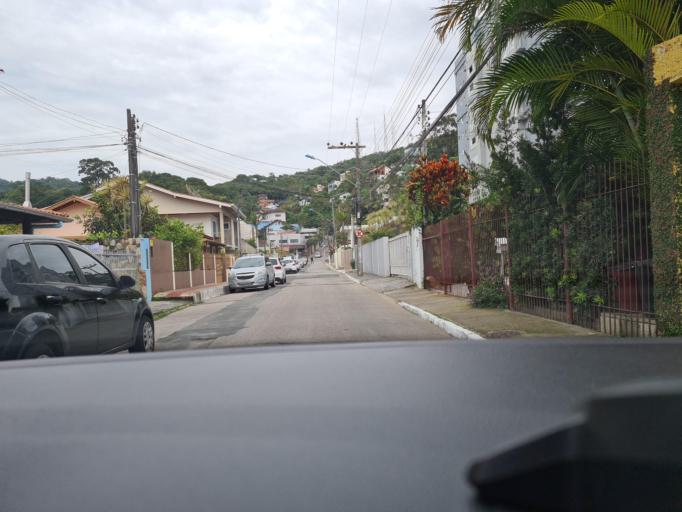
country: BR
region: Santa Catarina
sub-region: Itajai
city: Itajai
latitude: -26.9162
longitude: -48.6571
